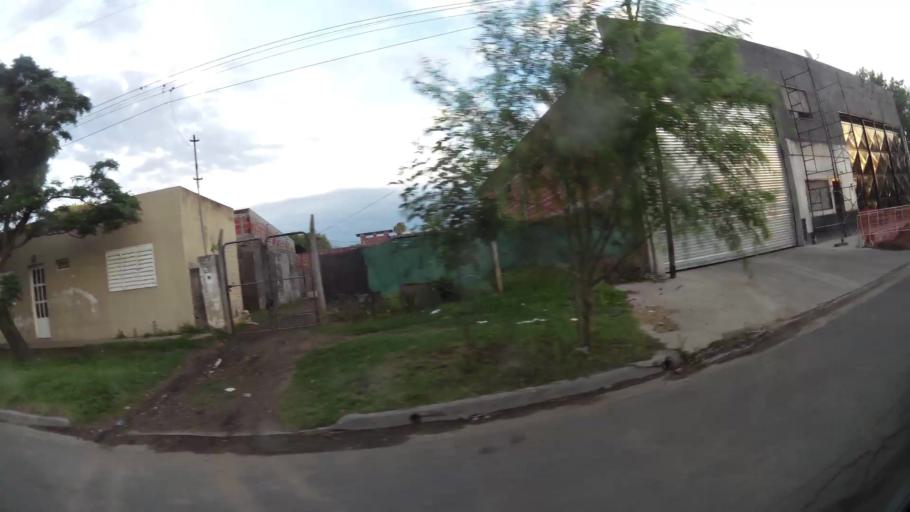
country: AR
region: Buenos Aires
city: San Nicolas de los Arroyos
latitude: -33.3155
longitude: -60.2375
